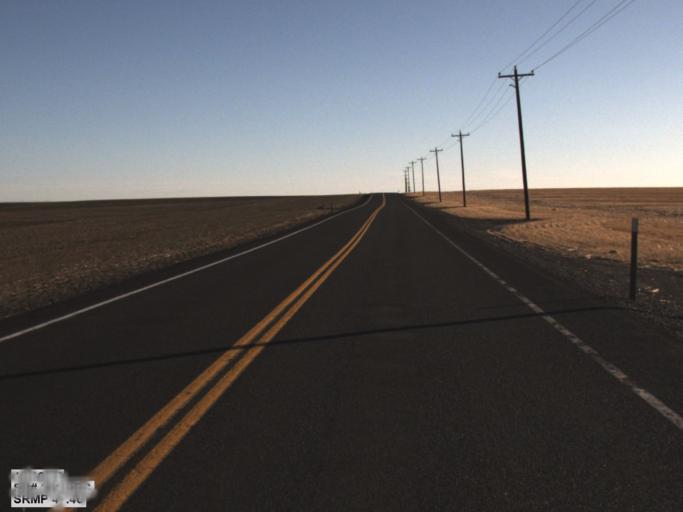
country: US
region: Washington
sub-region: Adams County
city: Ritzville
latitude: 46.9068
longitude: -118.3330
